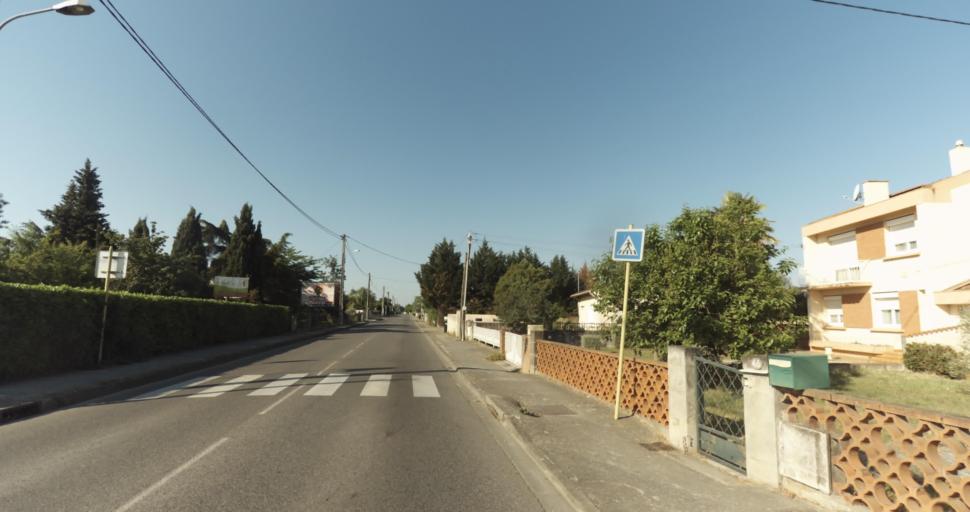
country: FR
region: Midi-Pyrenees
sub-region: Departement de la Haute-Garonne
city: La Salvetat-Saint-Gilles
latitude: 43.5724
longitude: 1.2694
